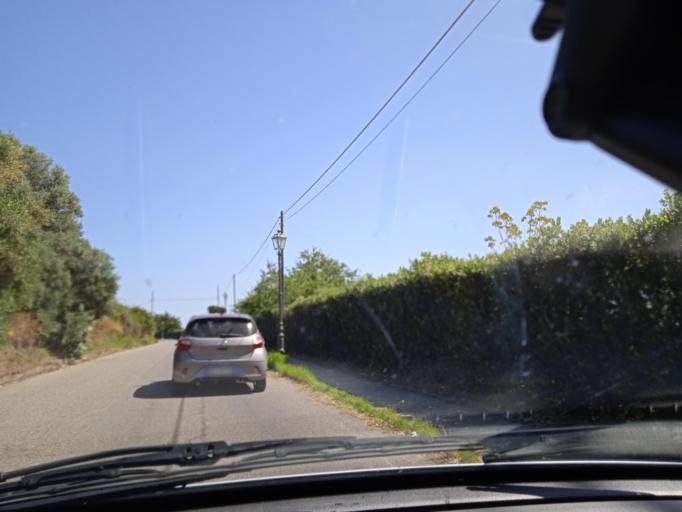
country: IT
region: Sicily
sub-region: Messina
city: Milazzo
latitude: 38.2336
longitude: 15.2489
